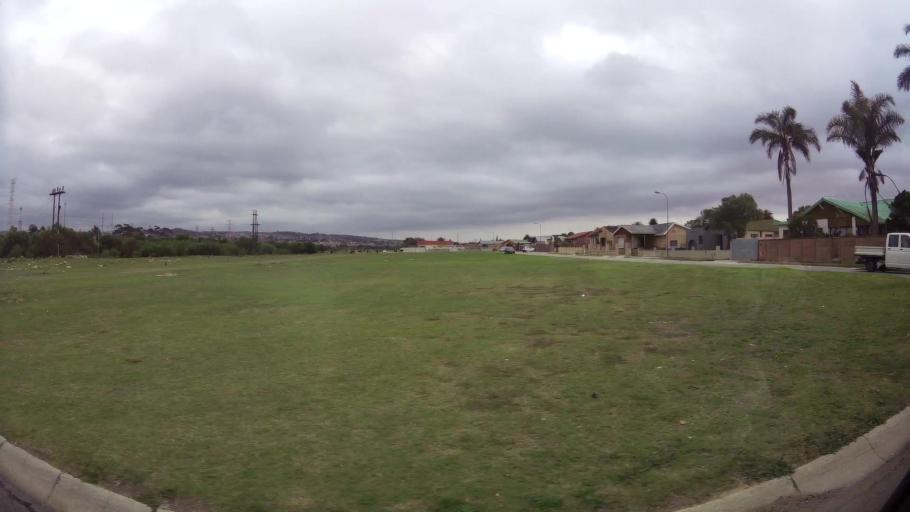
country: ZA
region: Eastern Cape
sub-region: Nelson Mandela Bay Metropolitan Municipality
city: Port Elizabeth
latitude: -33.9089
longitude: 25.5666
